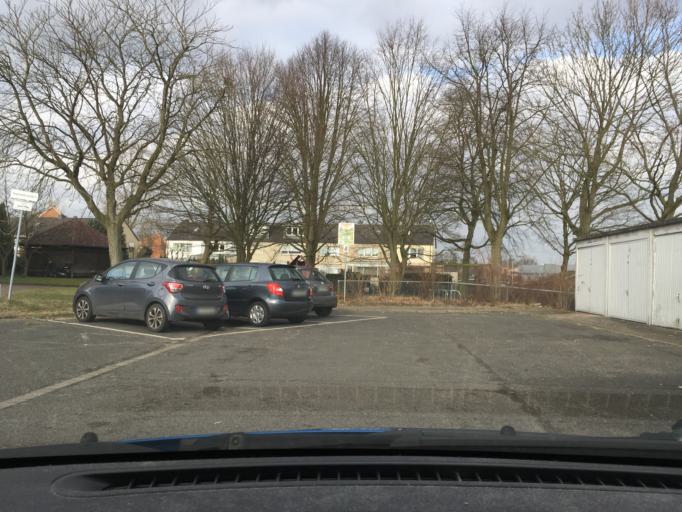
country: DE
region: Schleswig-Holstein
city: Wedel
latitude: 53.5738
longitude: 9.7258
